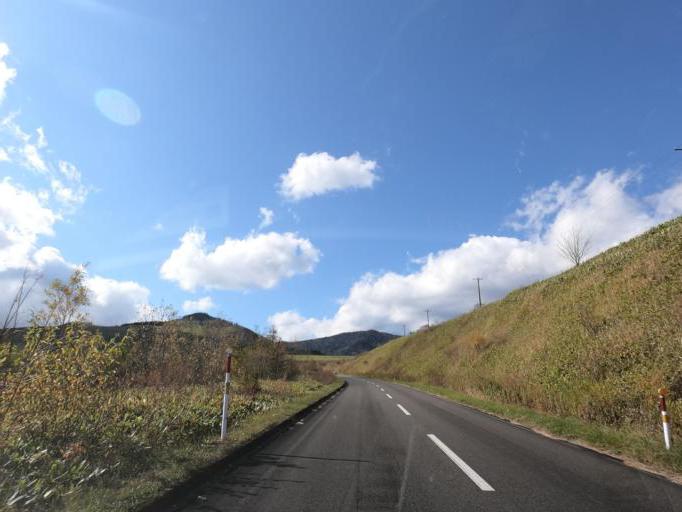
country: JP
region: Hokkaido
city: Otofuke
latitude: 43.2929
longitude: 143.1958
